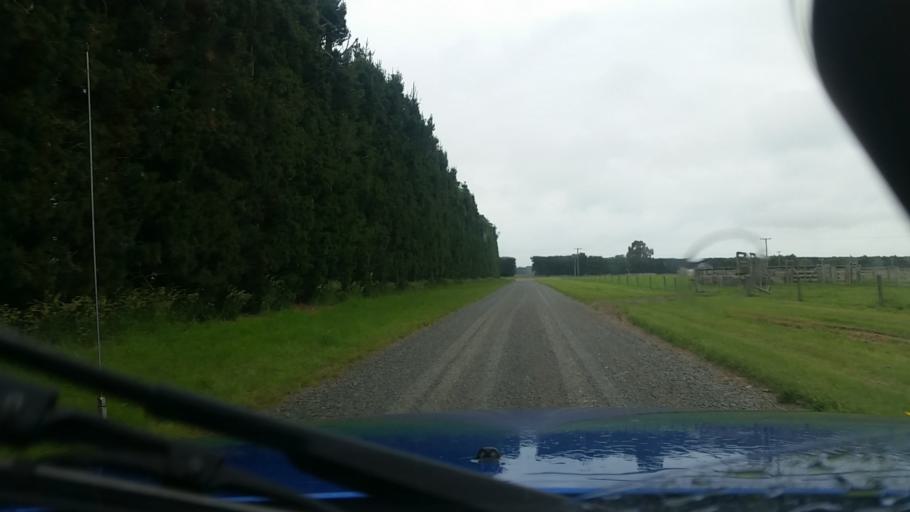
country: NZ
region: Canterbury
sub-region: Ashburton District
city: Tinwald
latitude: -43.9028
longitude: 171.5879
